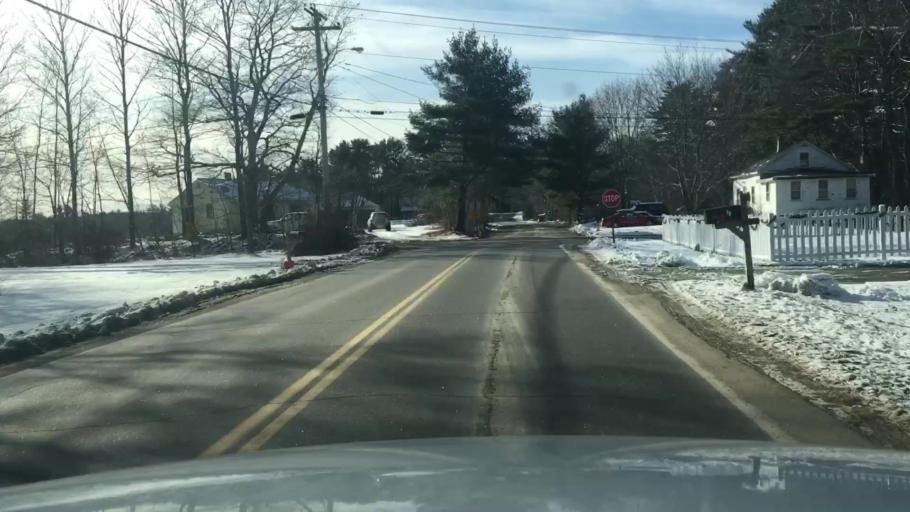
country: US
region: Maine
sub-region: Lincoln County
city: Wiscasset
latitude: 43.9626
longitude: -69.7000
